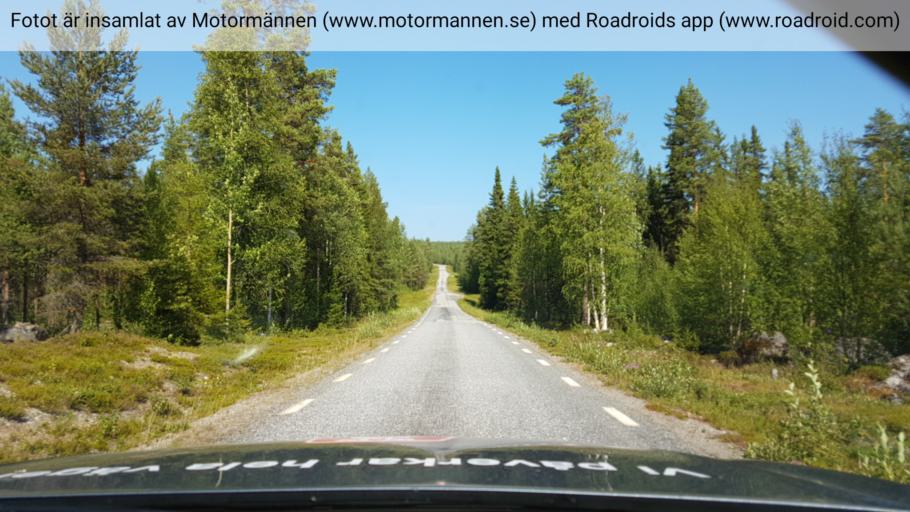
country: SE
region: Vaesterbotten
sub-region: Dorotea Kommun
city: Dorotea
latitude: 64.0263
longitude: 16.5153
